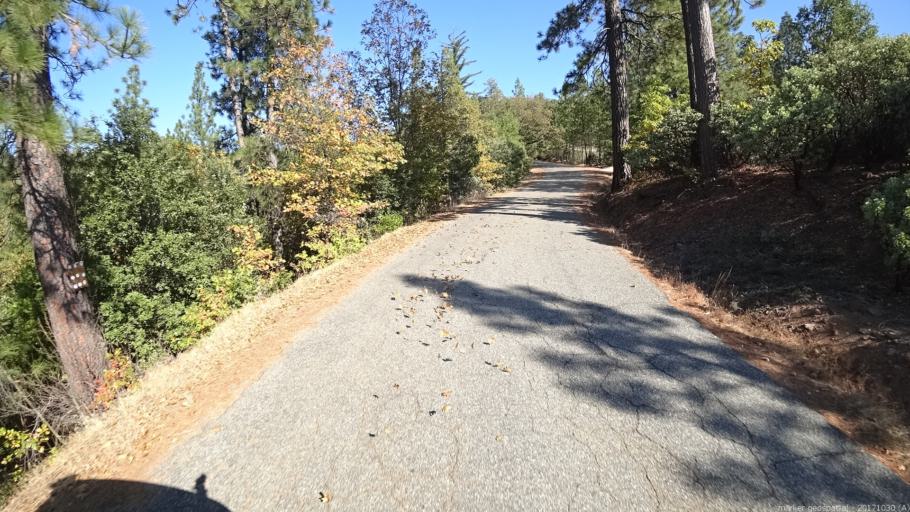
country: US
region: California
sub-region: Shasta County
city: Shingletown
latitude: 40.5765
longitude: -121.8790
